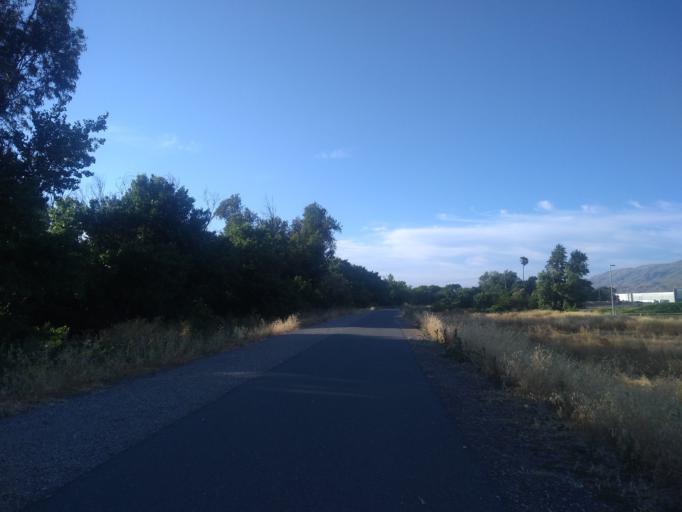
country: US
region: California
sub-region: Santa Clara County
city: Milpitas
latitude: 37.4293
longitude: -121.9281
